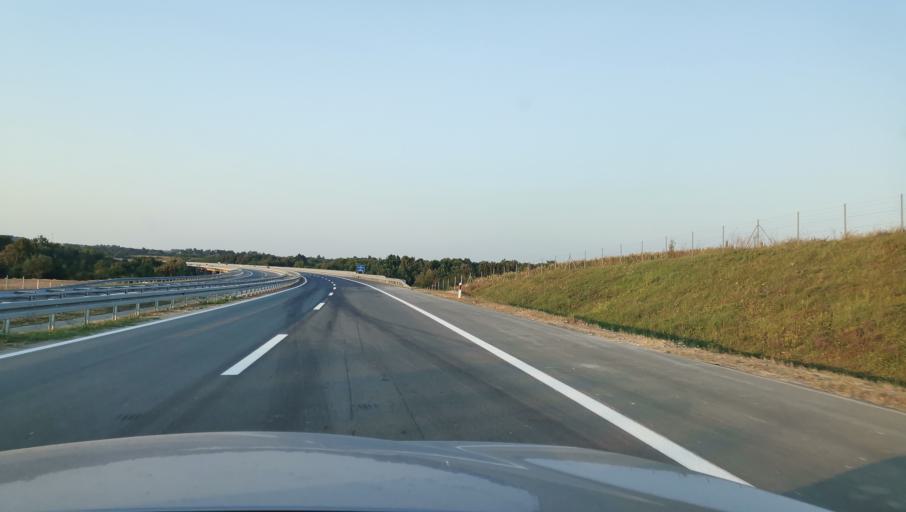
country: RS
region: Central Serbia
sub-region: Kolubarski Okrug
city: Ub
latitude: 44.4140
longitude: 20.1014
